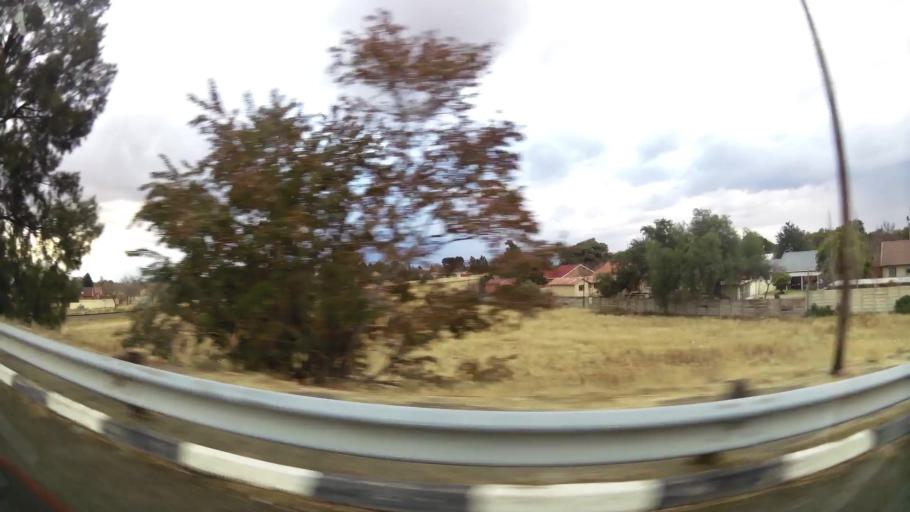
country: ZA
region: Orange Free State
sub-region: Lejweleputswa District Municipality
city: Welkom
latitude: -27.9587
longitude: 26.7271
